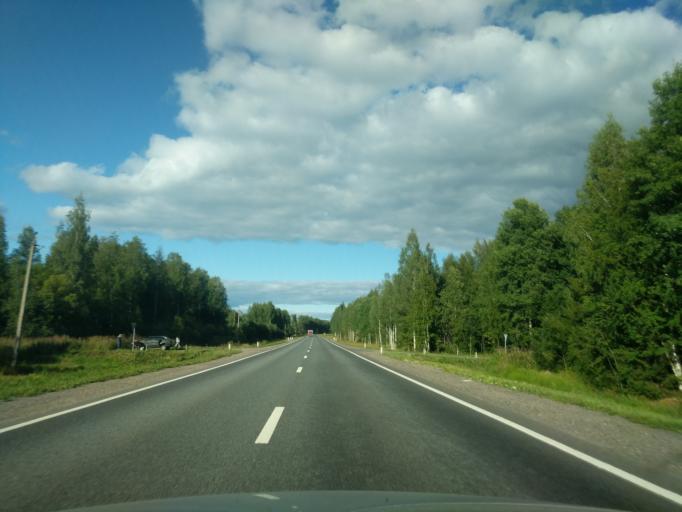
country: RU
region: Kostroma
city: Manturovo
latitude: 58.1501
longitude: 44.3726
